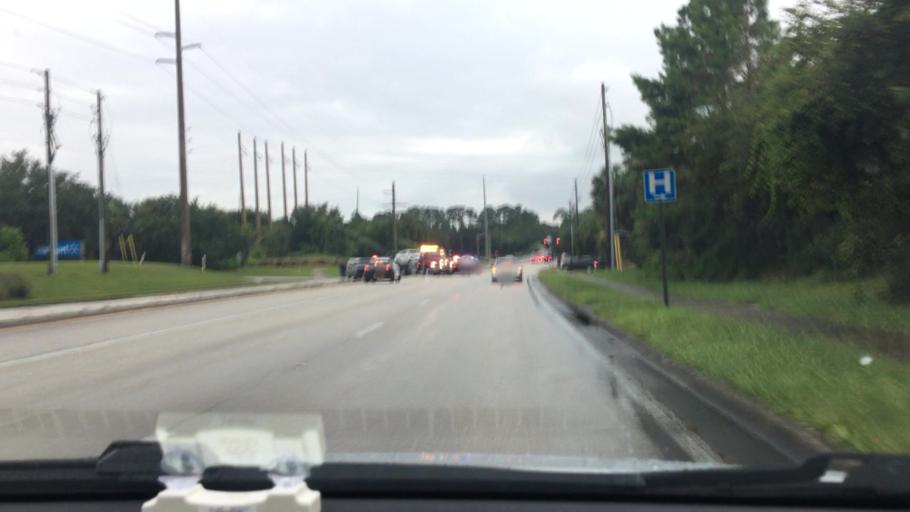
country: US
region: Florida
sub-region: Volusia County
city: Deltona
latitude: 28.9142
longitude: -81.2817
